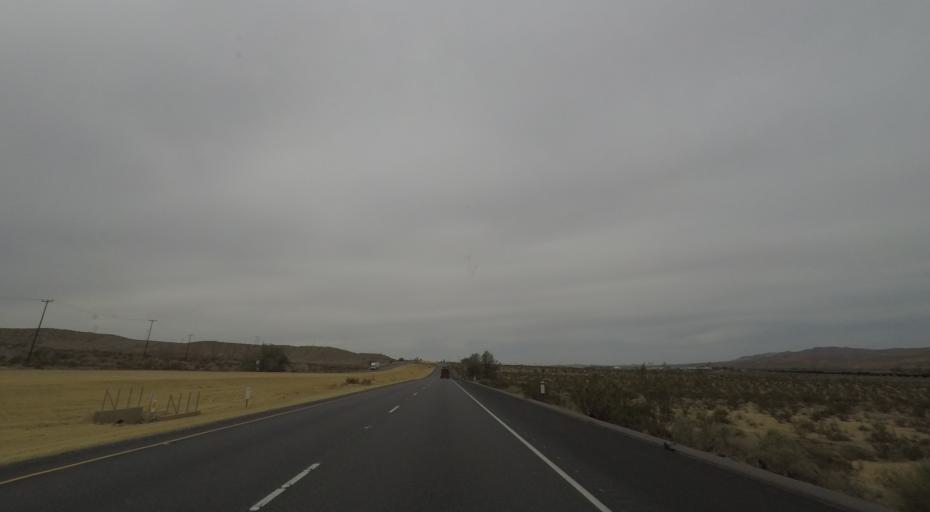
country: US
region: California
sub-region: San Bernardino County
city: Barstow
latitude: 34.8628
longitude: -116.9260
